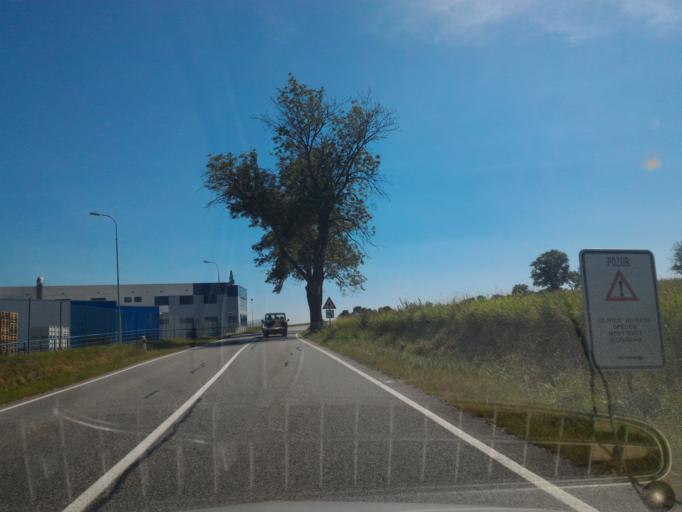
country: CZ
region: Vysocina
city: Dolni Cerekev
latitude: 49.3528
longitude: 15.4874
